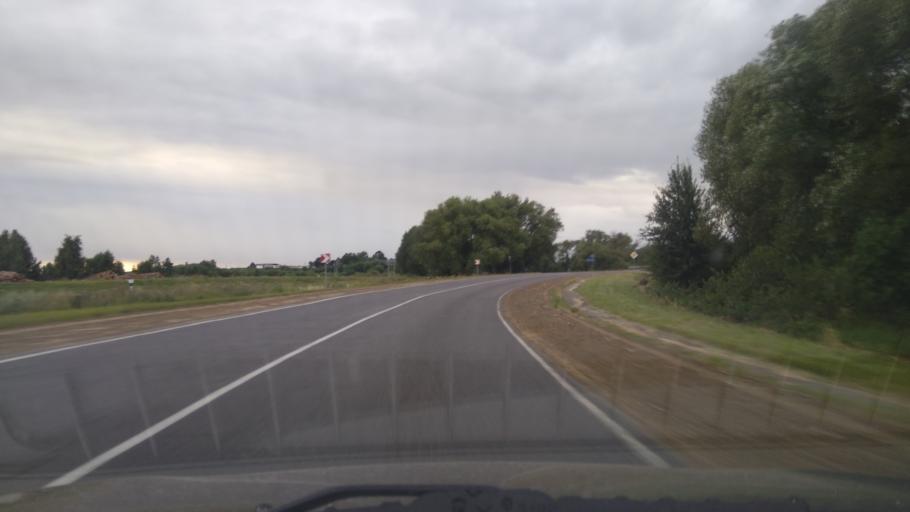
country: BY
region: Brest
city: Byaroza
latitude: 52.4173
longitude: 24.9802
